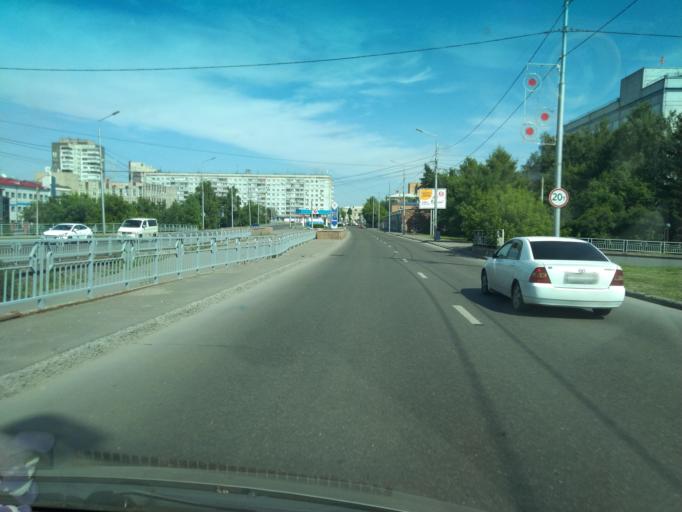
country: RU
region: Krasnoyarskiy
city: Krasnoyarsk
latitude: 56.0124
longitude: 92.8365
